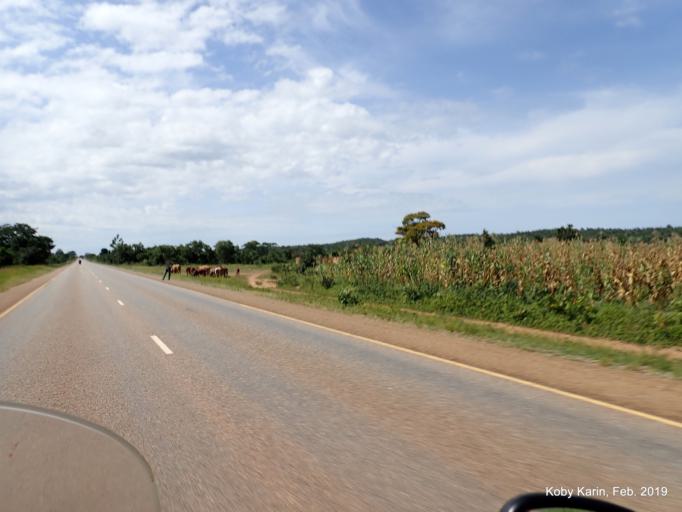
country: TZ
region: Geita
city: Uyovu
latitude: -3.1298
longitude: 31.3244
